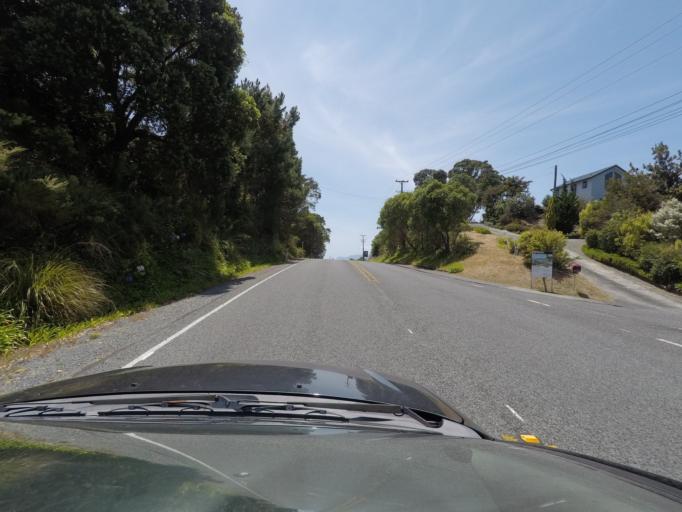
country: NZ
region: Auckland
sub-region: Auckland
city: Warkworth
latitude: -36.2951
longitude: 174.7984
